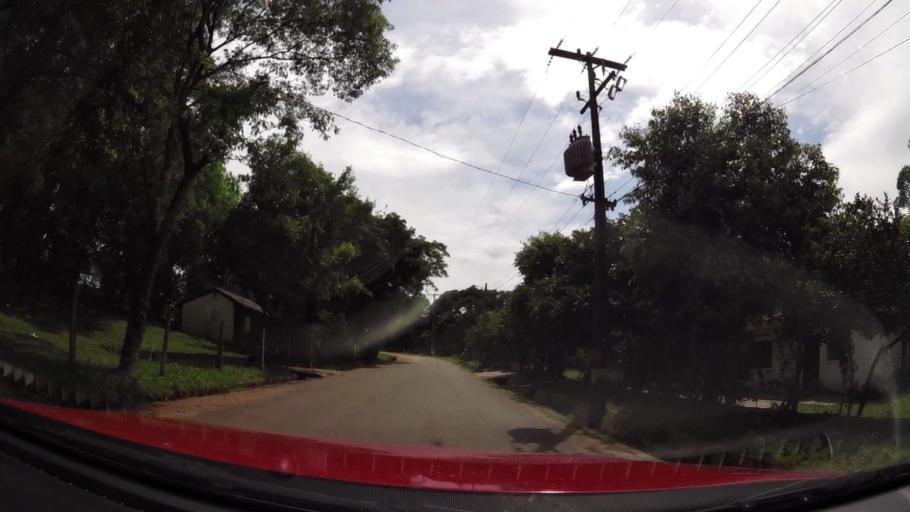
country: PY
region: Central
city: Limpio
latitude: -25.1784
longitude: -57.4423
